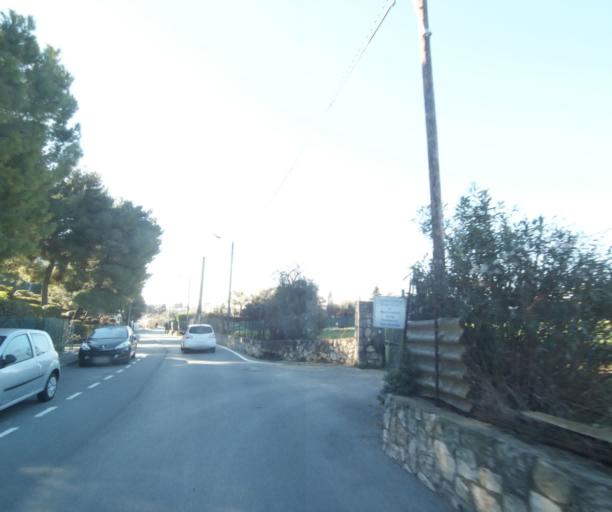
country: FR
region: Provence-Alpes-Cote d'Azur
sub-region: Departement des Alpes-Maritimes
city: Antibes
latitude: 43.5812
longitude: 7.0945
